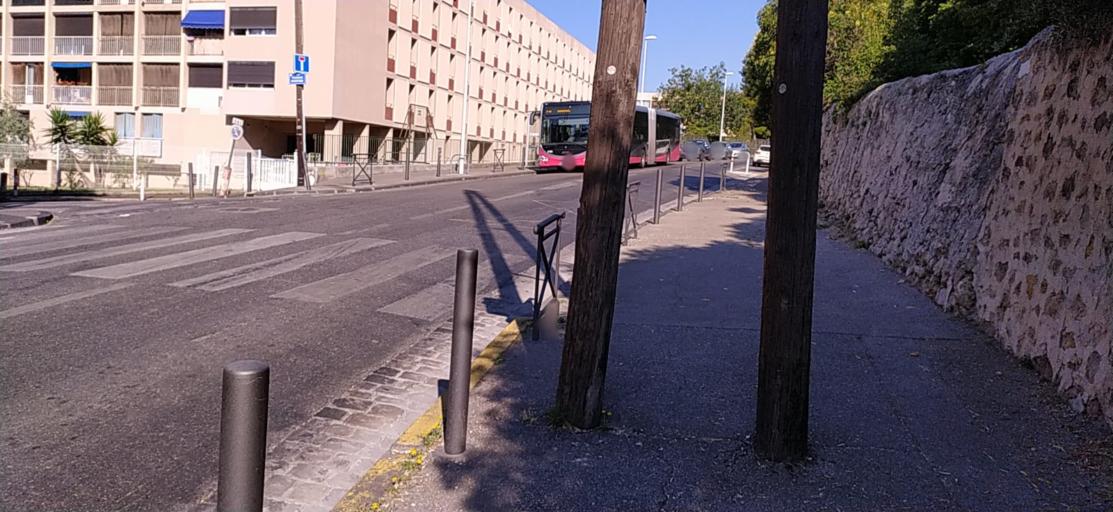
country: FR
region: Provence-Alpes-Cote d'Azur
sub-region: Departement des Bouches-du-Rhone
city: Marseille 14
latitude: 43.3395
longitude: 5.3556
